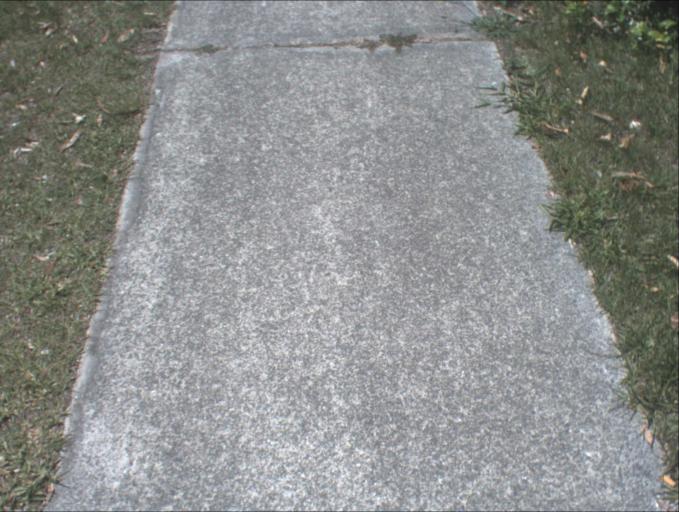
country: AU
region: Queensland
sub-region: Logan
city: Woodridge
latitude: -27.6241
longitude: 153.1069
